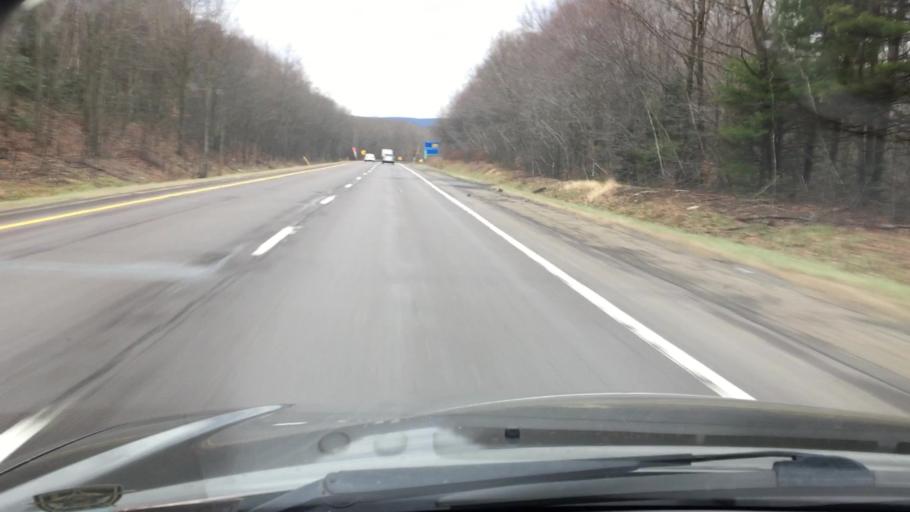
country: US
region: Pennsylvania
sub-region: Luzerne County
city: White Haven
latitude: 41.0586
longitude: -75.7187
